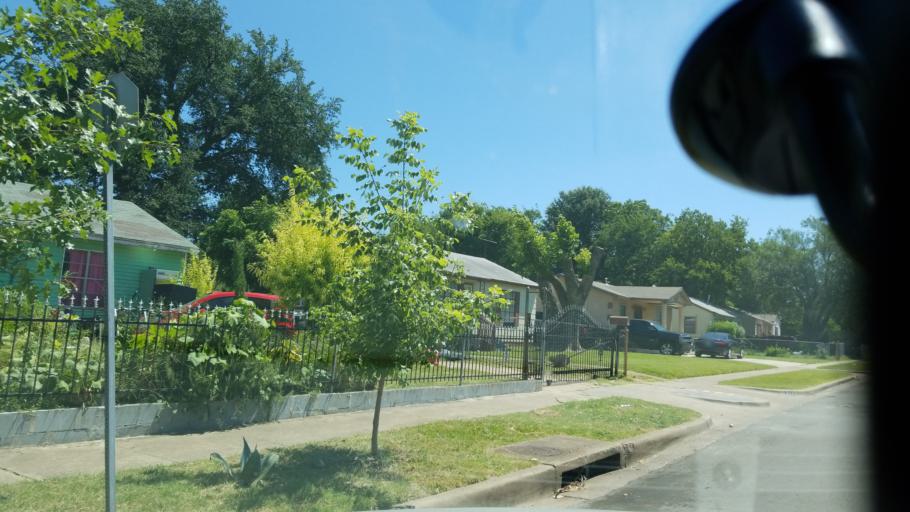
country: US
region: Texas
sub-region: Dallas County
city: Cockrell Hill
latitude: 32.7122
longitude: -96.8261
